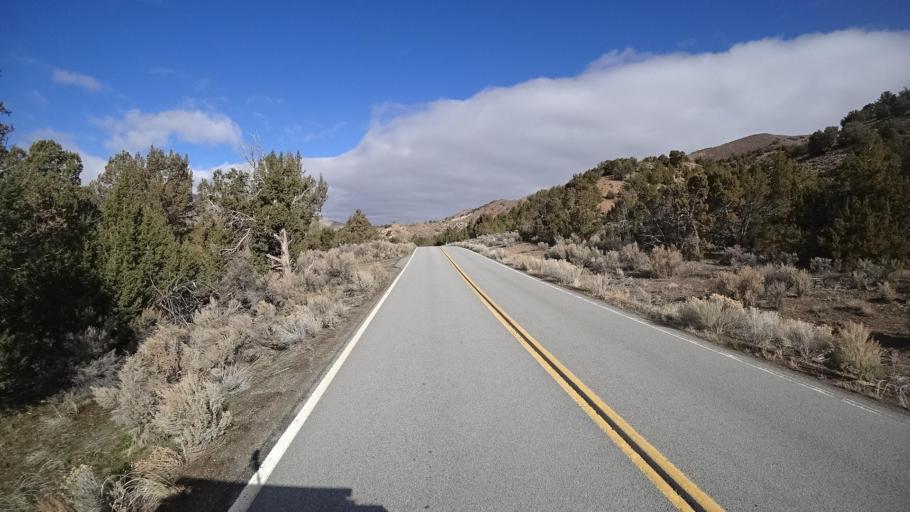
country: US
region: Nevada
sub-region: Washoe County
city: Cold Springs
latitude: 39.9052
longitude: -120.0003
